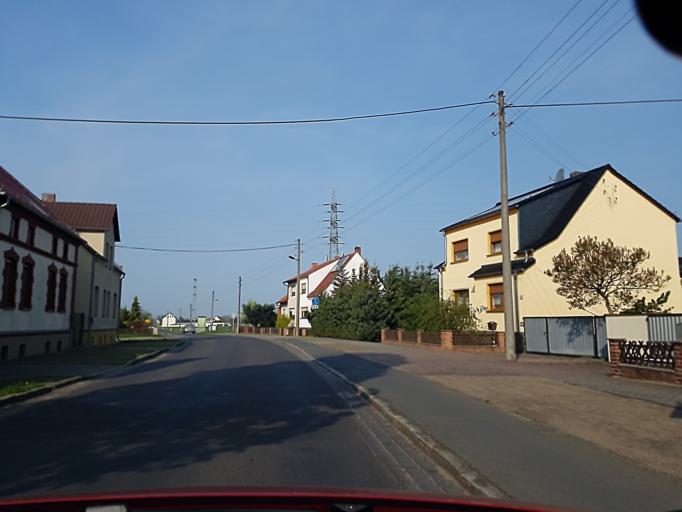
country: DE
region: Brandenburg
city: Falkenberg
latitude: 51.5871
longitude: 13.2253
